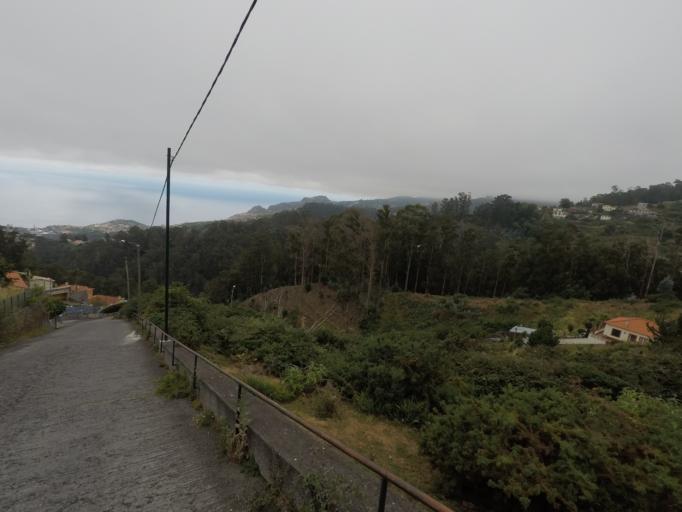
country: PT
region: Madeira
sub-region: Camara de Lobos
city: Curral das Freiras
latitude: 32.6853
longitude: -16.9487
